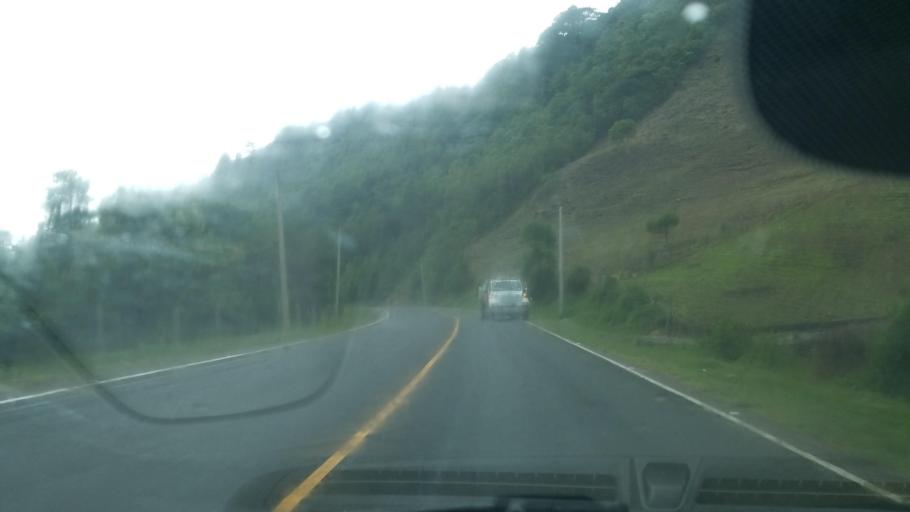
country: HN
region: Ocotepeque
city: La Labor
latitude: 14.4684
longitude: -89.0903
